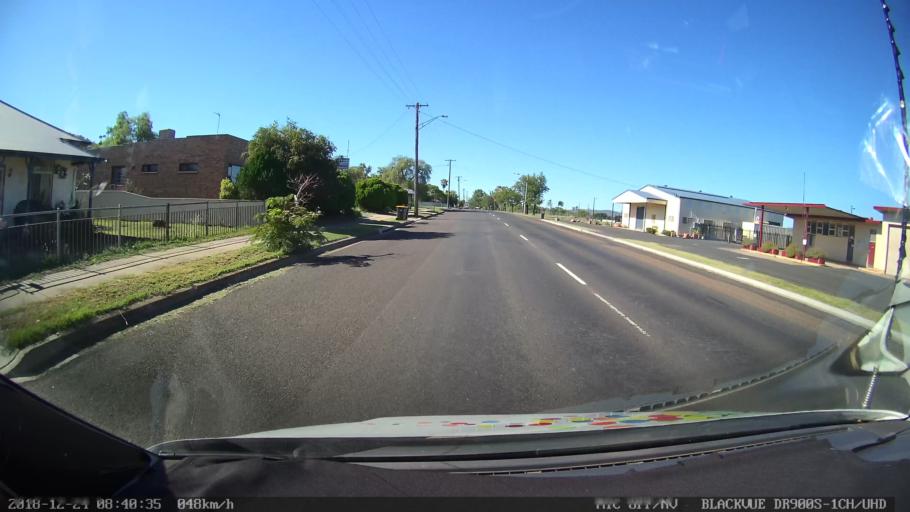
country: AU
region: New South Wales
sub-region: Liverpool Plains
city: Quirindi
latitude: -31.3560
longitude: 150.6463
